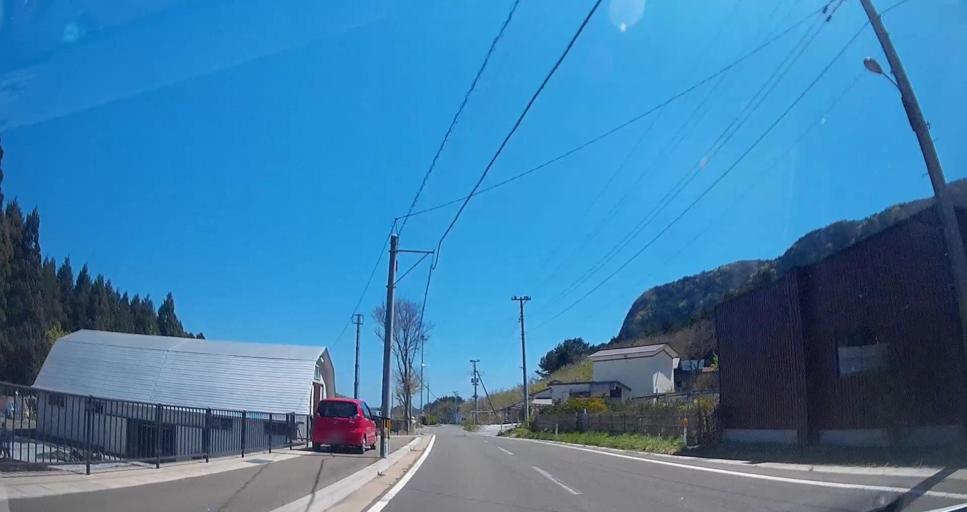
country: JP
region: Aomori
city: Mutsu
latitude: 41.3983
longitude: 141.4491
